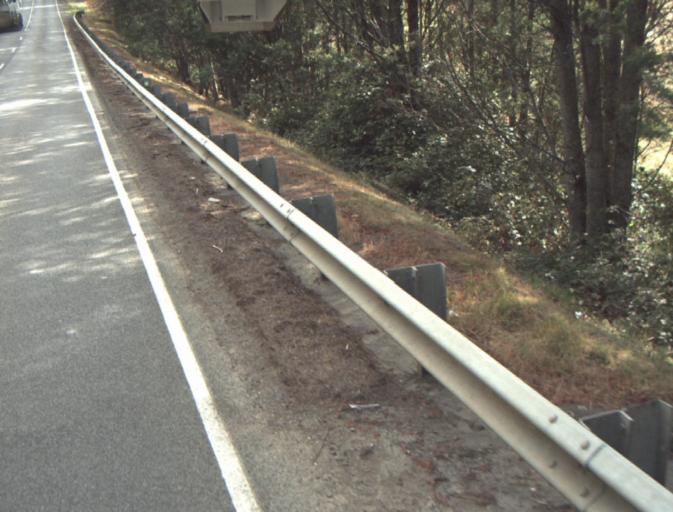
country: AU
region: Tasmania
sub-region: Launceston
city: Mayfield
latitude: -41.2953
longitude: 147.2138
